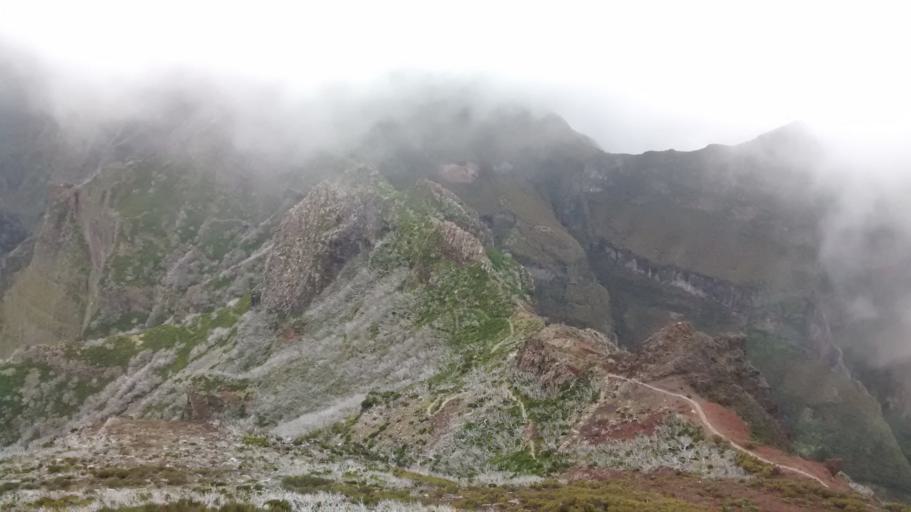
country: PT
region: Madeira
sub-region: Camara de Lobos
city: Curral das Freiras
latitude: 32.7591
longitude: -16.9431
